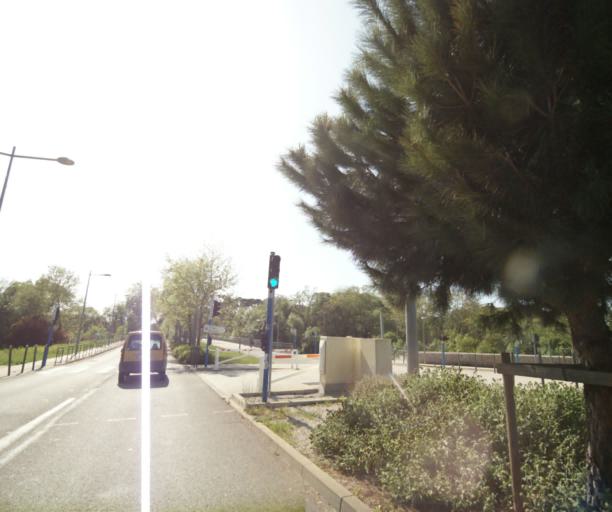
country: FR
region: Languedoc-Roussillon
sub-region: Departement de l'Herault
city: Juvignac
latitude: 43.6156
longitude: 3.8186
